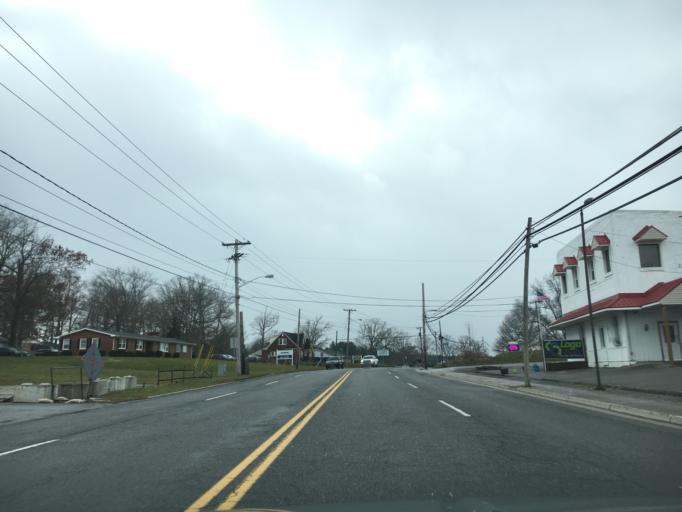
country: US
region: Virginia
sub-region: Montgomery County
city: Christiansburg
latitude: 37.1311
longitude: -80.3943
